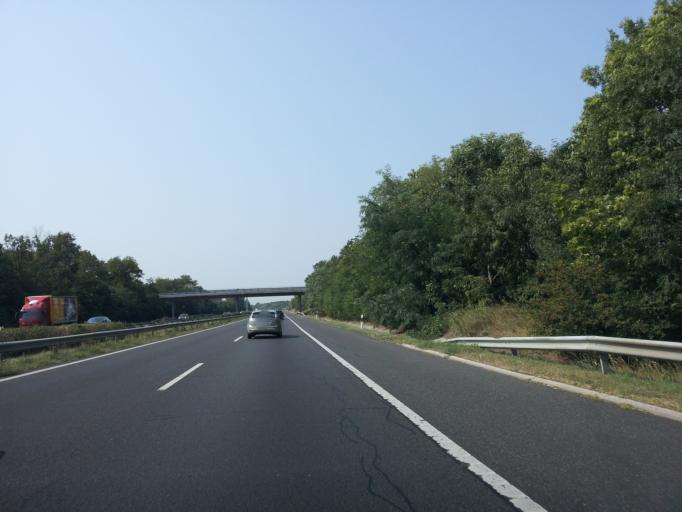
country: HU
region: Fejer
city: Martonvasar
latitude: 47.3222
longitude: 18.7634
